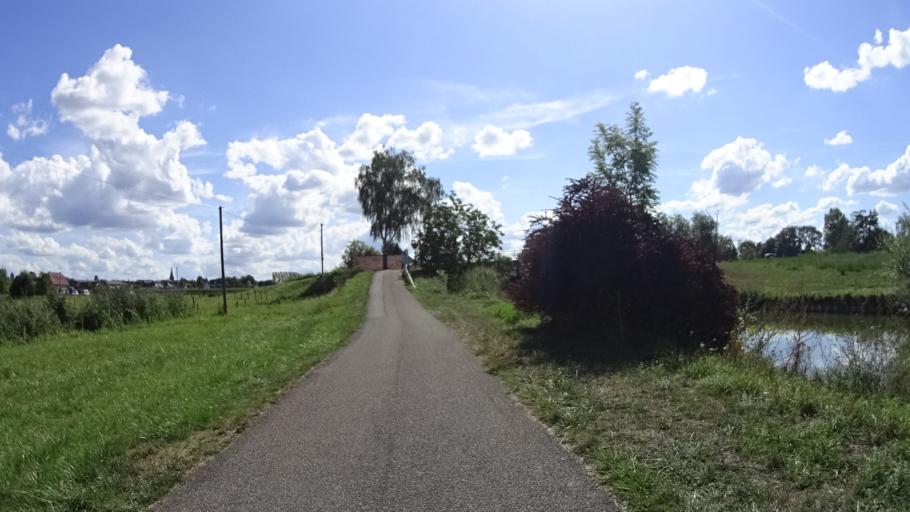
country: FR
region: Alsace
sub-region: Departement du Haut-Rhin
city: Dannemarie
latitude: 47.6417
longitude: 7.1227
